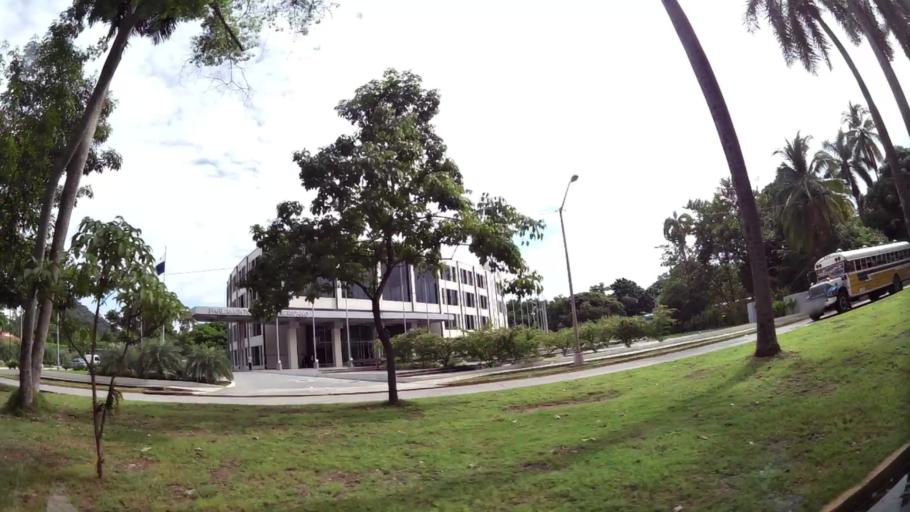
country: PA
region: Panama
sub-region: Distrito de Panama
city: Ancon
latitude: 8.9434
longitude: -79.5537
